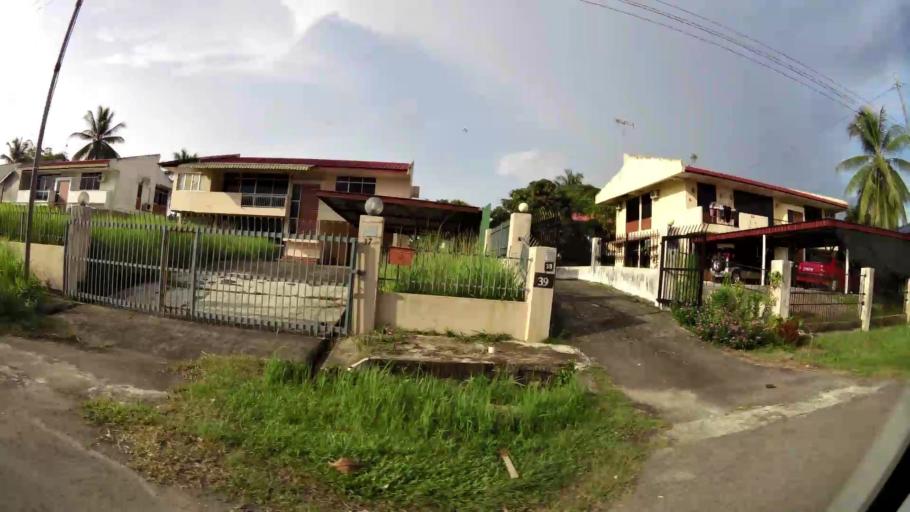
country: BN
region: Brunei and Muara
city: Bandar Seri Begawan
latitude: 4.9662
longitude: 114.9814
